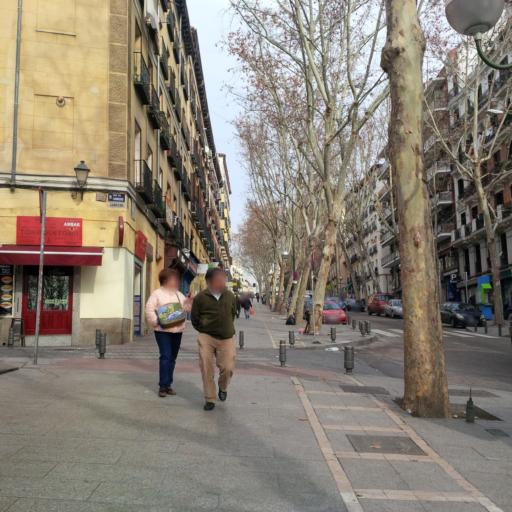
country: ES
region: Madrid
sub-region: Provincia de Madrid
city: Madrid
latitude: 40.4084
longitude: -3.7074
